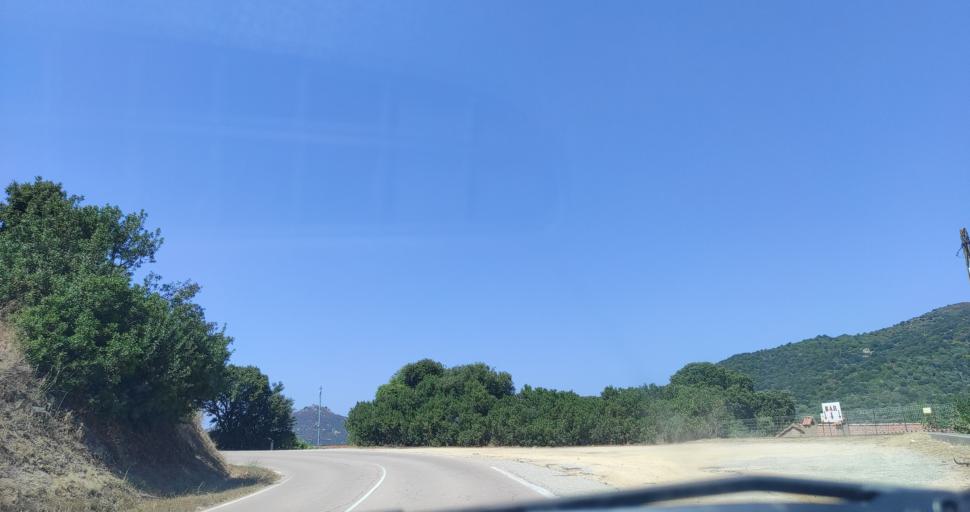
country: FR
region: Corsica
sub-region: Departement de la Corse-du-Sud
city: Alata
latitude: 41.9616
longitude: 8.7274
